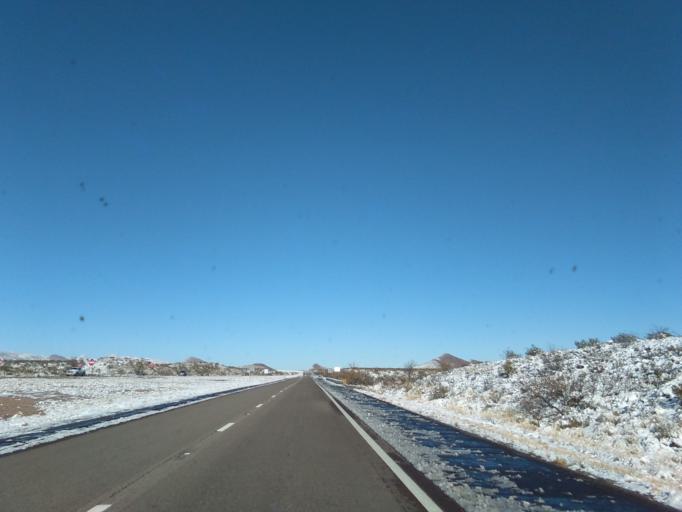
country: US
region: New Mexico
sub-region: Socorro County
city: Socorro
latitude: 33.7252
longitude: -107.0239
